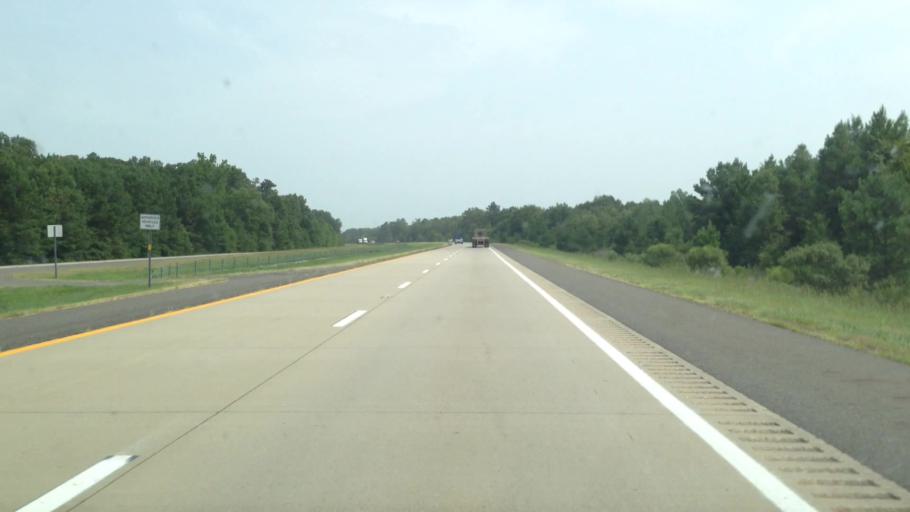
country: US
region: Texas
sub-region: Bowie County
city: Texarkana
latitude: 33.2081
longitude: -93.8750
